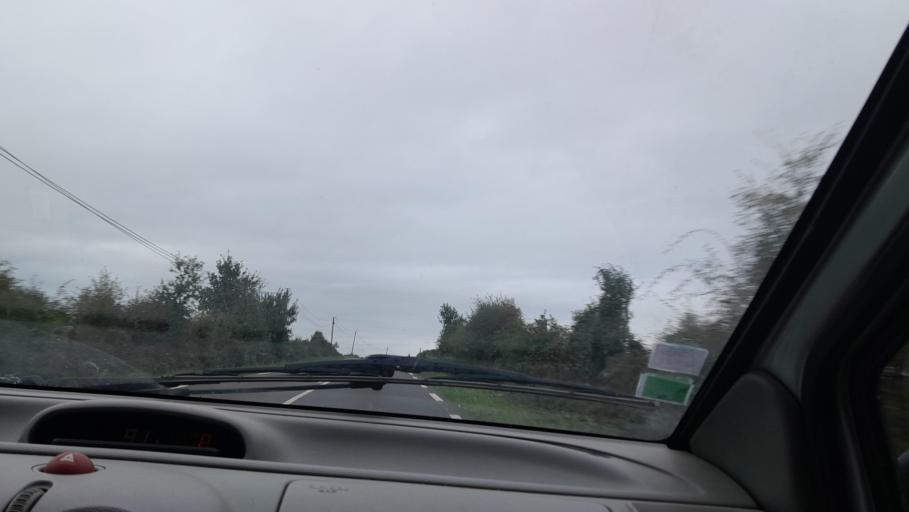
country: FR
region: Pays de la Loire
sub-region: Departement de Maine-et-Loire
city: Pouance
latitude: 47.6371
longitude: -1.2024
